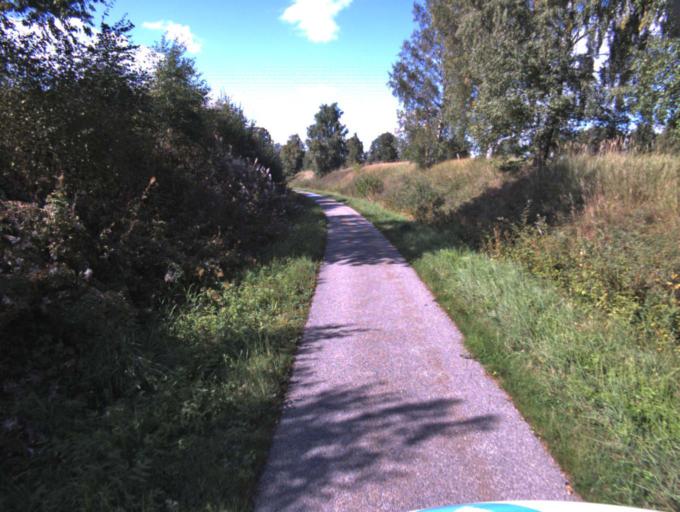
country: SE
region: Vaestra Goetaland
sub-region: Ulricehamns Kommun
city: Ulricehamn
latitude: 57.8441
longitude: 13.3009
